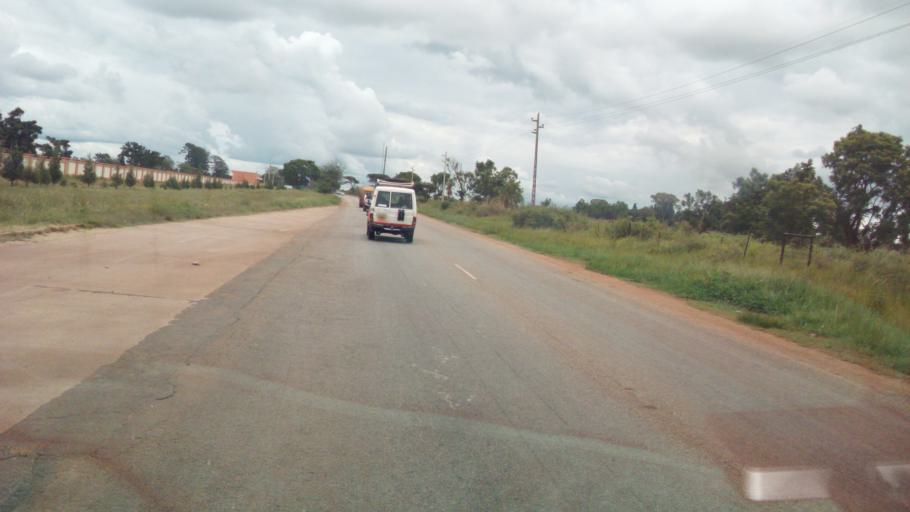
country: ZW
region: Harare
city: Harare
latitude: -17.7315
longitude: 31.0229
